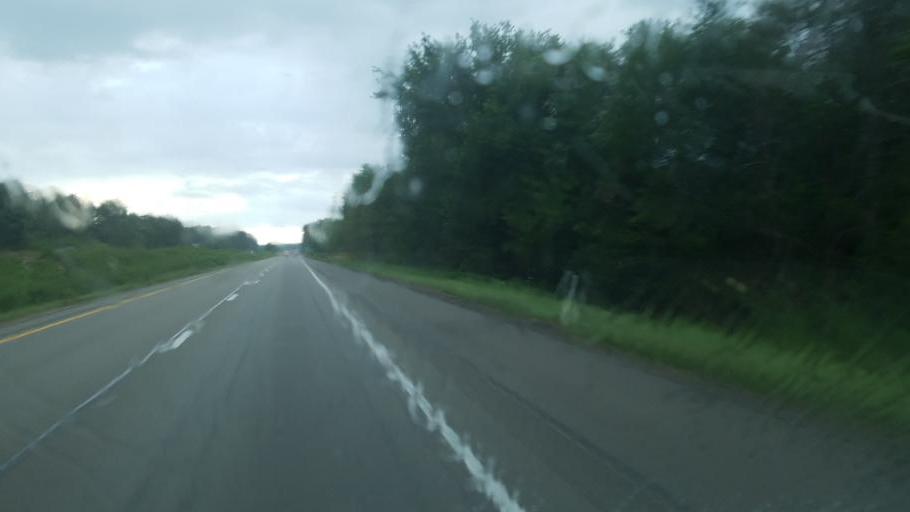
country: US
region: Pennsylvania
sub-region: Mercer County
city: Grove City
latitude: 41.1717
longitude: -80.1657
